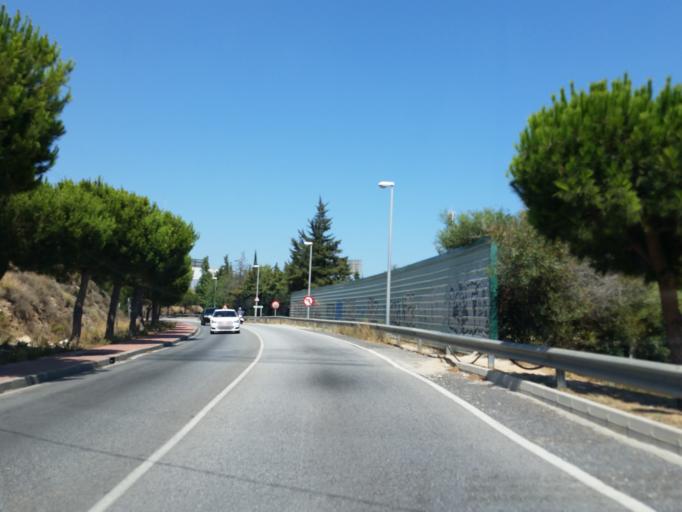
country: ES
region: Andalusia
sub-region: Provincia de Malaga
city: Benalmadena
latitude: 36.6092
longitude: -4.5366
